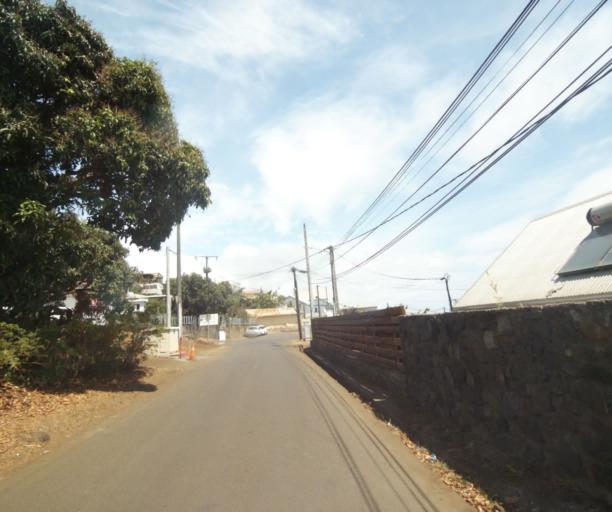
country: RE
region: Reunion
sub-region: Reunion
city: Trois-Bassins
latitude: -21.0994
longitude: 55.2776
